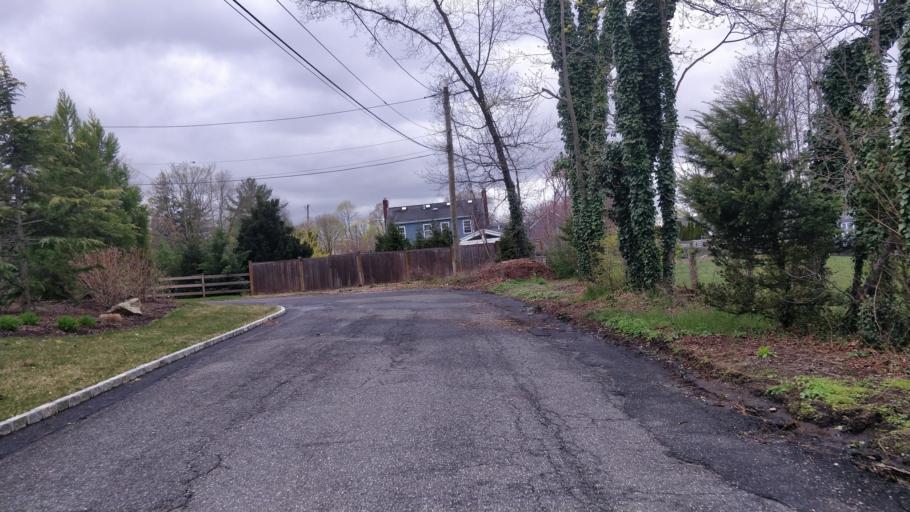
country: US
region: New York
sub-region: Suffolk County
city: East Setauket
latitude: 40.9488
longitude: -73.0958
